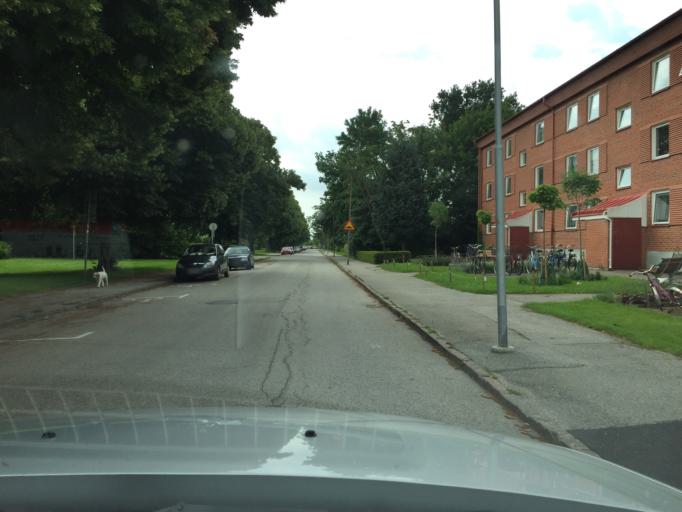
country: SE
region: Skane
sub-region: Lunds Kommun
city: Lund
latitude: 55.7019
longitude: 13.1655
